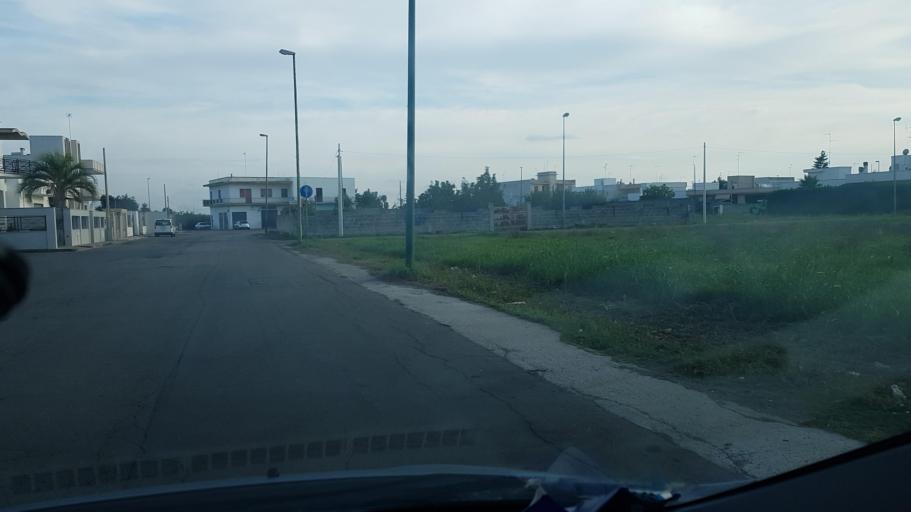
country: IT
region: Apulia
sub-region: Provincia di Lecce
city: Veglie
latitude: 40.3336
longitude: 17.9743
